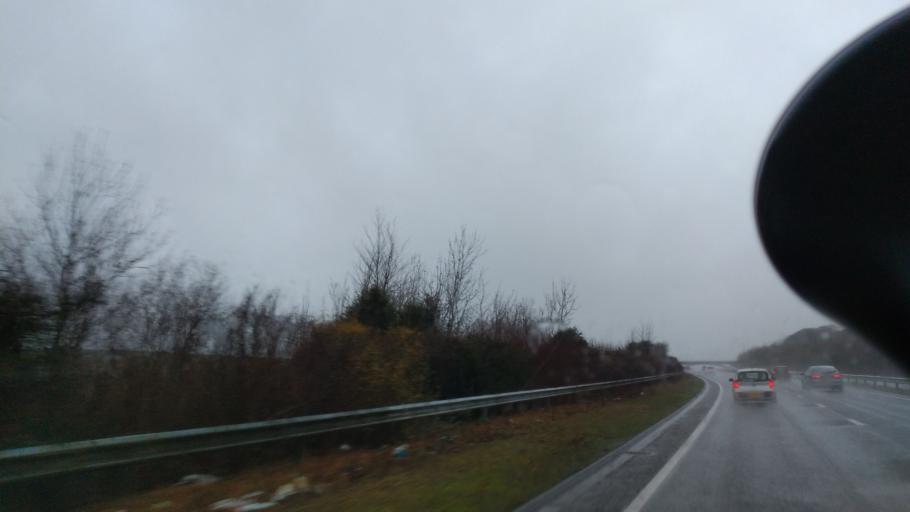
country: GB
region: England
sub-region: Brighton and Hove
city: Brighton
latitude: 50.8674
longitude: -0.1116
